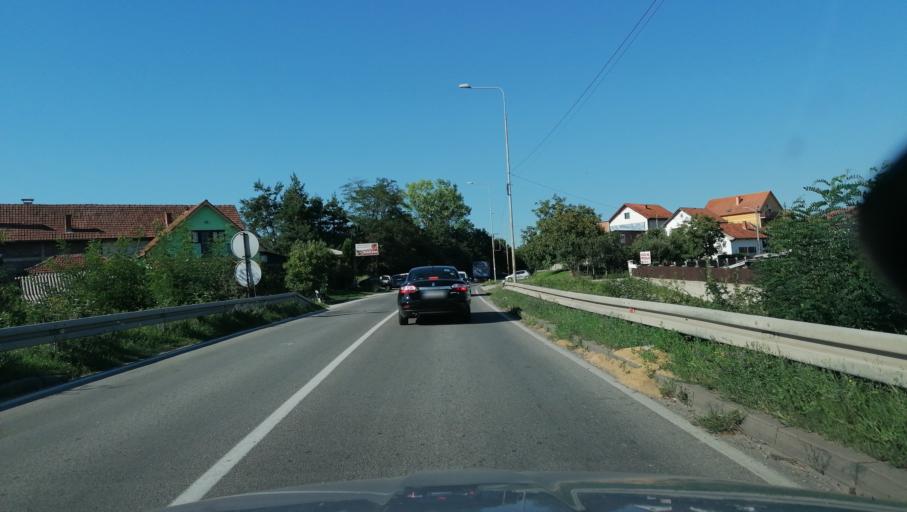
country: RS
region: Central Serbia
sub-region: Raski Okrug
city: Kraljevo
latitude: 43.7271
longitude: 20.6485
